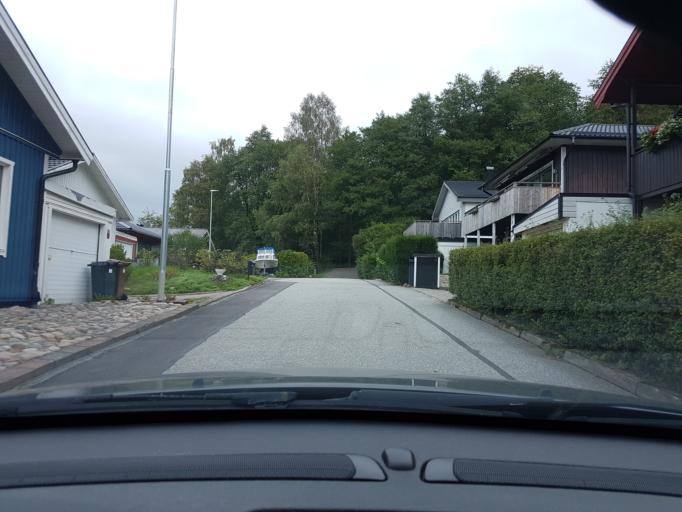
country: SE
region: Vaestra Goetaland
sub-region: Ale Kommun
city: Alafors
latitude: 57.9114
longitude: 12.0719
